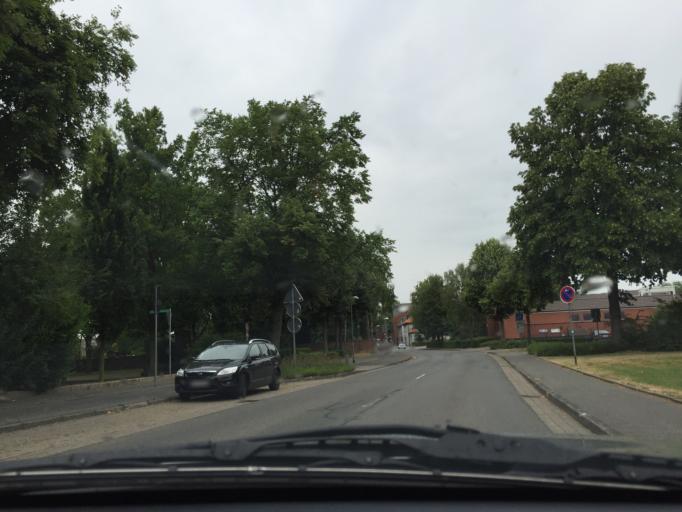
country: DE
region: North Rhine-Westphalia
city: Rees
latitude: 51.7604
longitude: 6.3929
